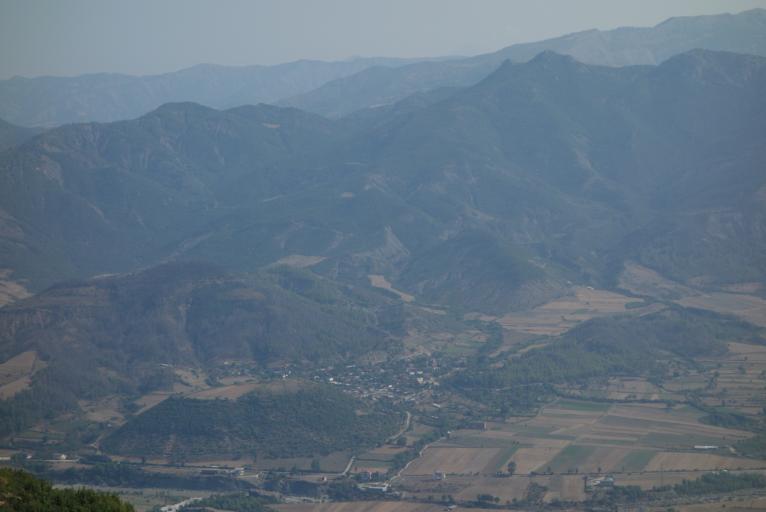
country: AL
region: Gjirokaster
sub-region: Rrethi i Permetit
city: Permet
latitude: 40.2224
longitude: 20.3360
